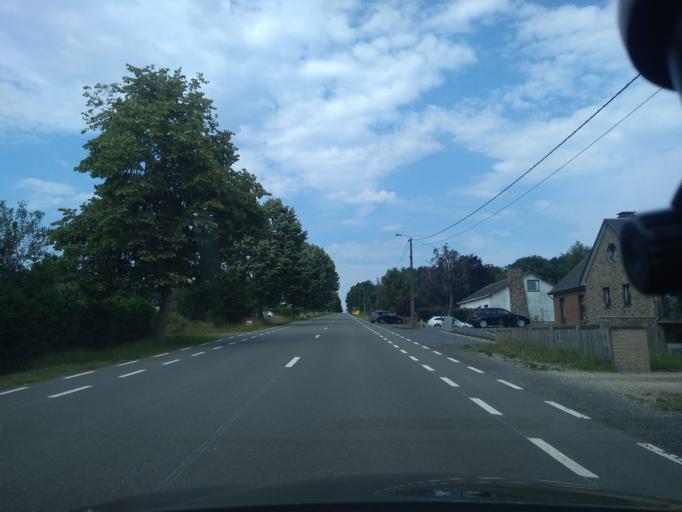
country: BE
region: Wallonia
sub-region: Province du Luxembourg
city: Libin
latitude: 49.9917
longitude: 5.2649
